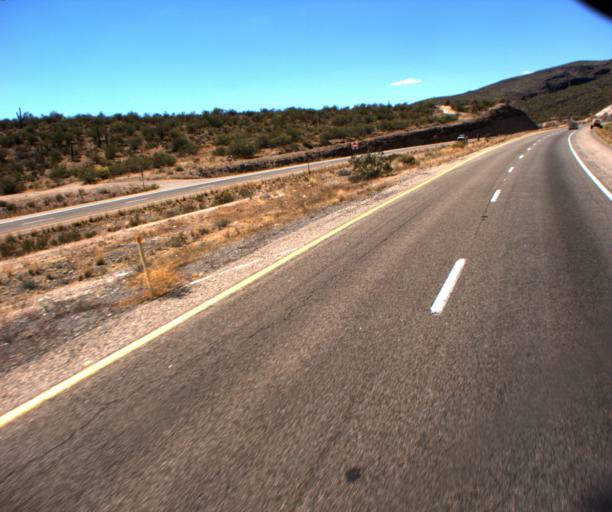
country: US
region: Arizona
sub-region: Yavapai County
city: Bagdad
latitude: 34.5611
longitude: -113.4567
